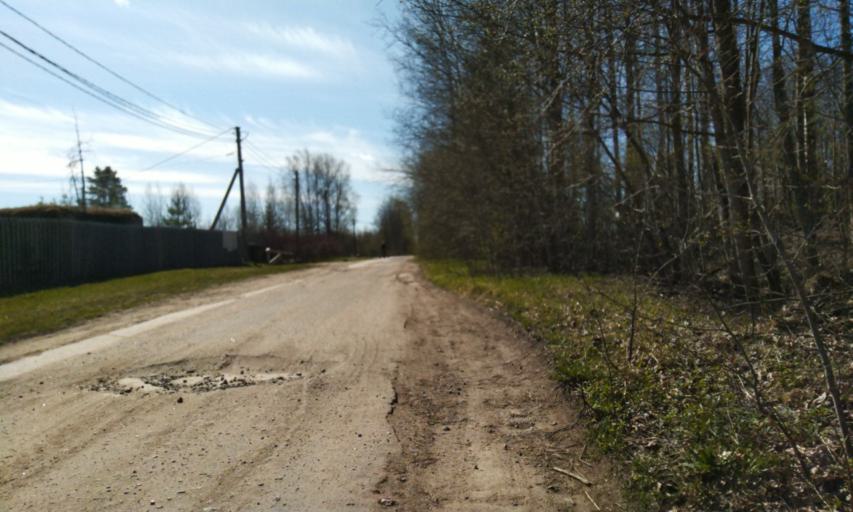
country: RU
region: Leningrad
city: Garbolovo
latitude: 60.3904
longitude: 30.4803
